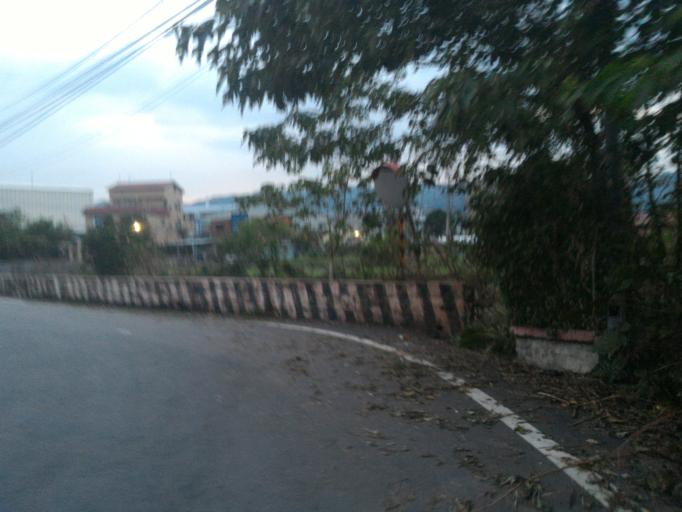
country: TW
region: Taiwan
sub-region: Taoyuan
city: Taoyuan
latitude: 24.9592
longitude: 121.3942
